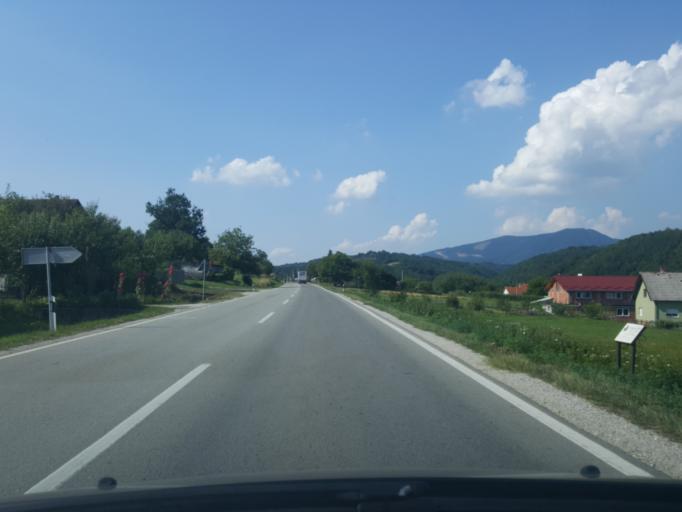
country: RS
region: Central Serbia
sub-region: Moravicki Okrug
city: Gornji Milanovac
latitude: 44.0635
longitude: 20.4913
